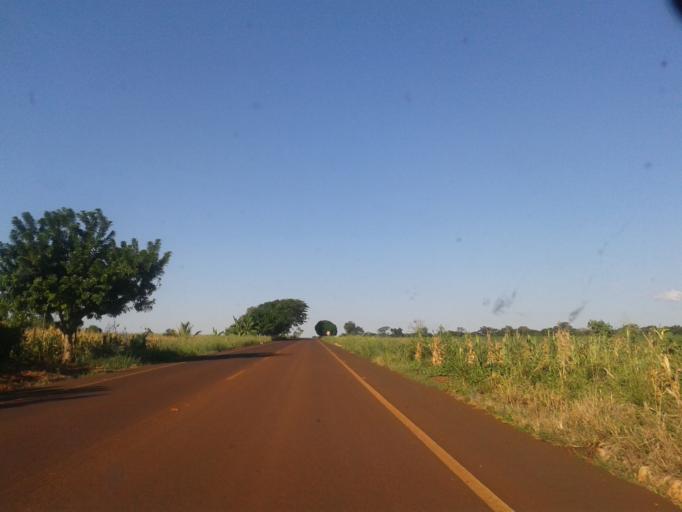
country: BR
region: Minas Gerais
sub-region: Santa Vitoria
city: Santa Vitoria
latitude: -18.6954
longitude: -49.9313
